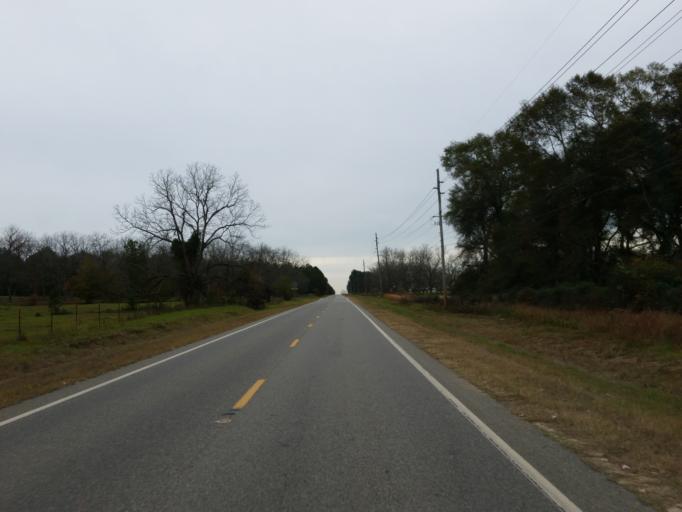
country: US
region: Georgia
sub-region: Crisp County
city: Cordele
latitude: 31.9248
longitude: -83.7203
